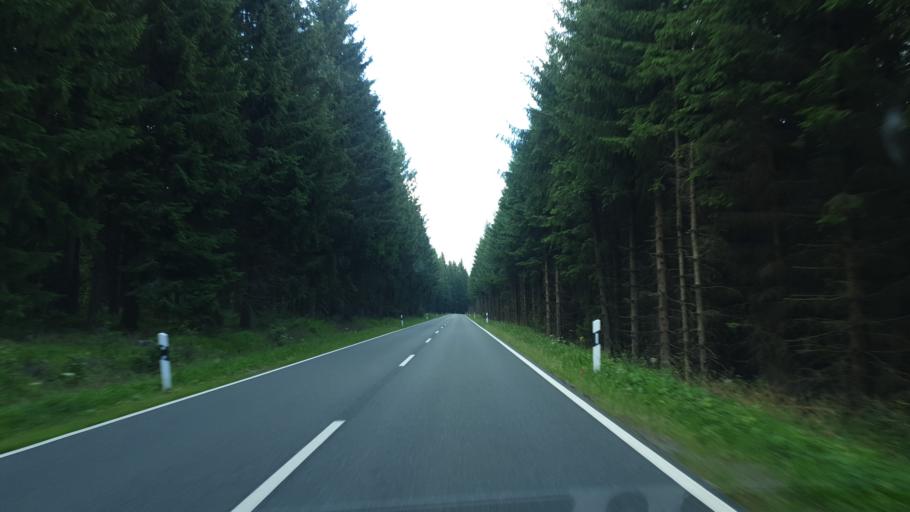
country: DE
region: Saxony
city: Hammerbrucke
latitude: 50.4432
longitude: 12.4203
